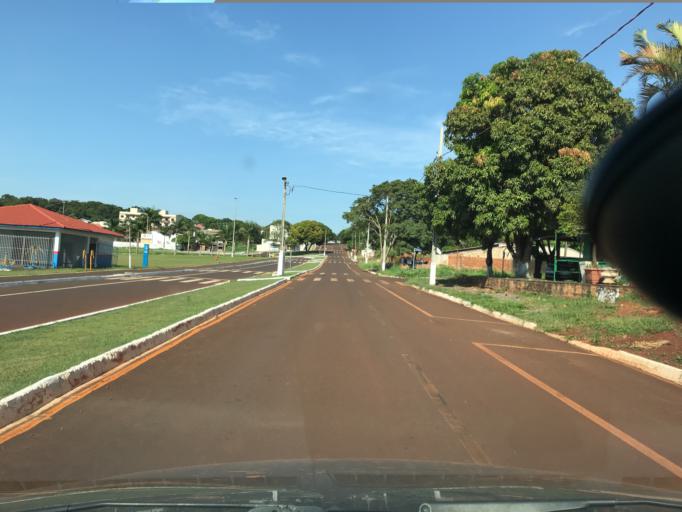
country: BR
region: Parana
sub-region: Palotina
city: Palotina
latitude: -24.2877
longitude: -53.8310
